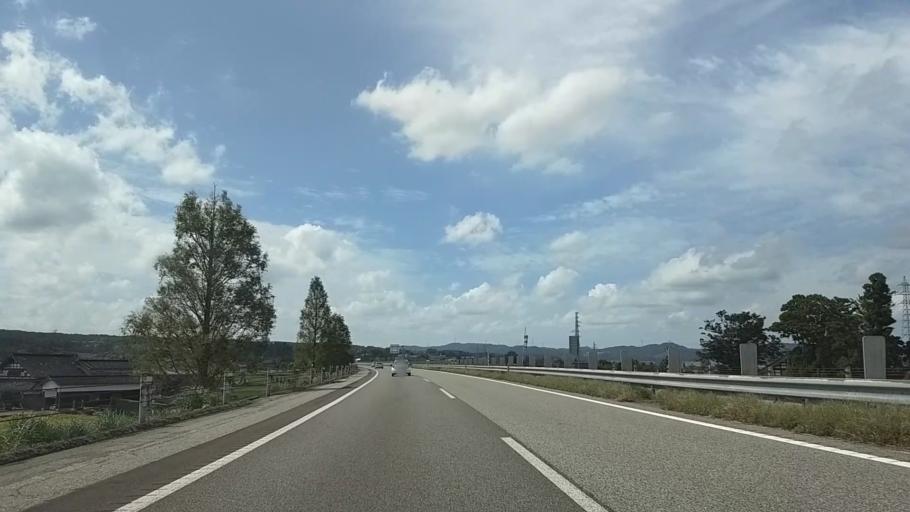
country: JP
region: Toyama
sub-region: Oyabe Shi
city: Oyabe
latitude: 36.6317
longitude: 136.8910
